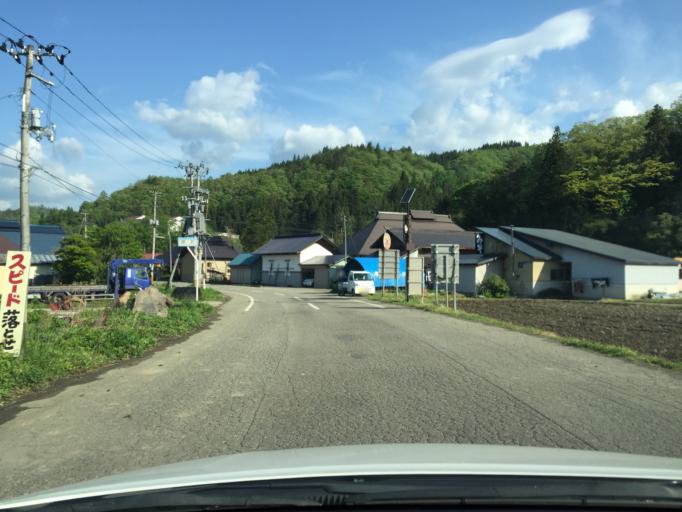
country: JP
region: Fukushima
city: Kitakata
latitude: 37.6775
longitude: 139.7966
